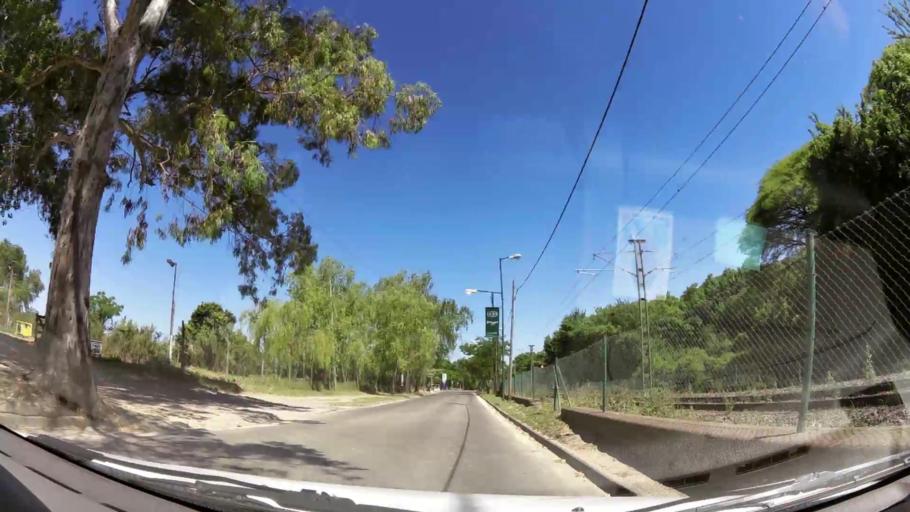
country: AR
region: Buenos Aires
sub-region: Partido de San Isidro
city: San Isidro
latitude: -34.4800
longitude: -58.4832
